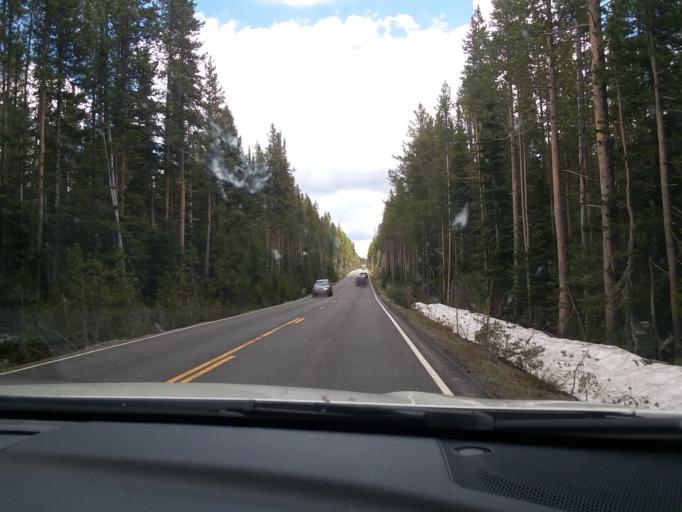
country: US
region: Idaho
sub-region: Teton County
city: Driggs
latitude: 44.1771
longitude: -110.6609
